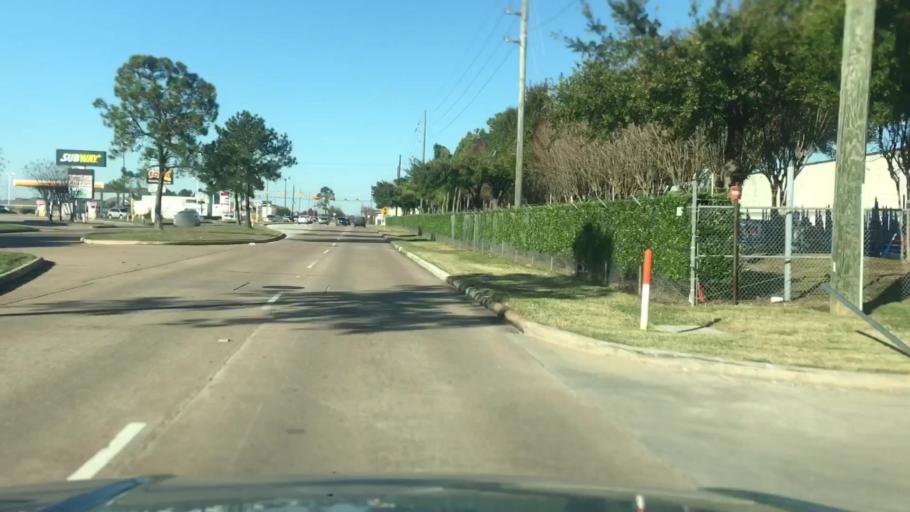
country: US
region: Texas
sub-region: Fort Bend County
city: Cinco Ranch
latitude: 29.8001
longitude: -95.7519
